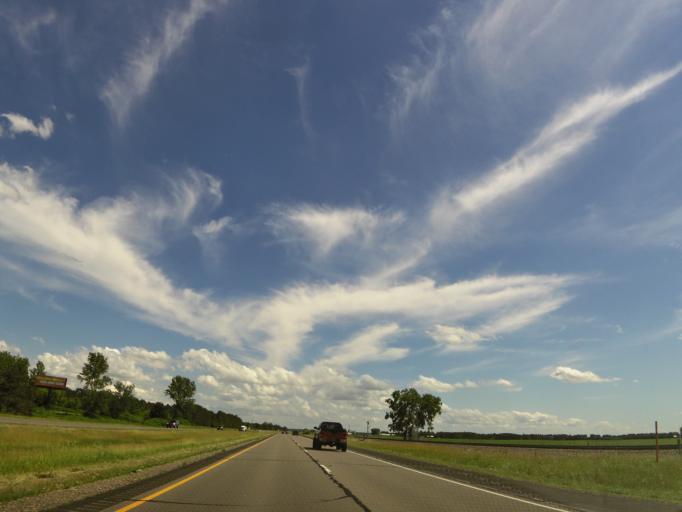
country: US
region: Minnesota
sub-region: Benton County
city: Rice
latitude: 45.7325
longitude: -94.2009
